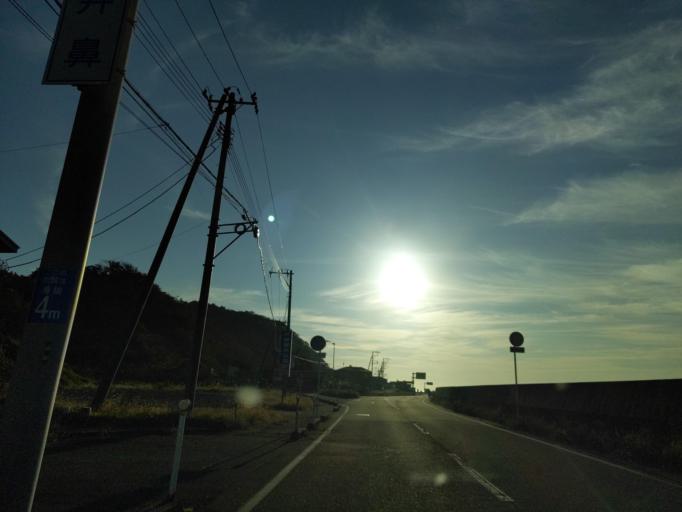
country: JP
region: Niigata
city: Nagaoka
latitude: 37.5541
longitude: 138.7072
